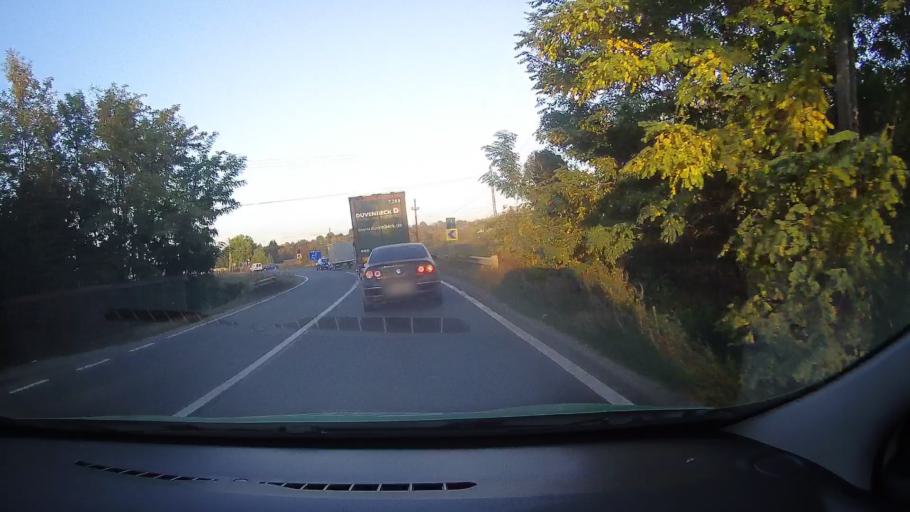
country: RO
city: Dioszeg
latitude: 47.2918
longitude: 22.0093
